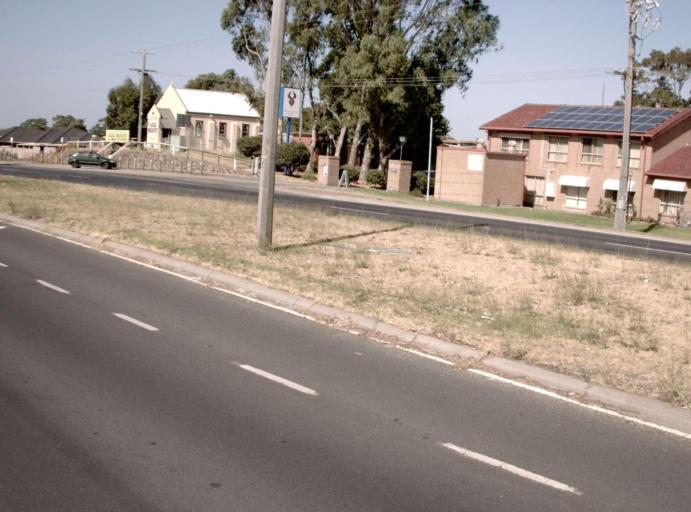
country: AU
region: Victoria
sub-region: Frankston
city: Carrum Downs
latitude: -38.0925
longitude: 145.1782
